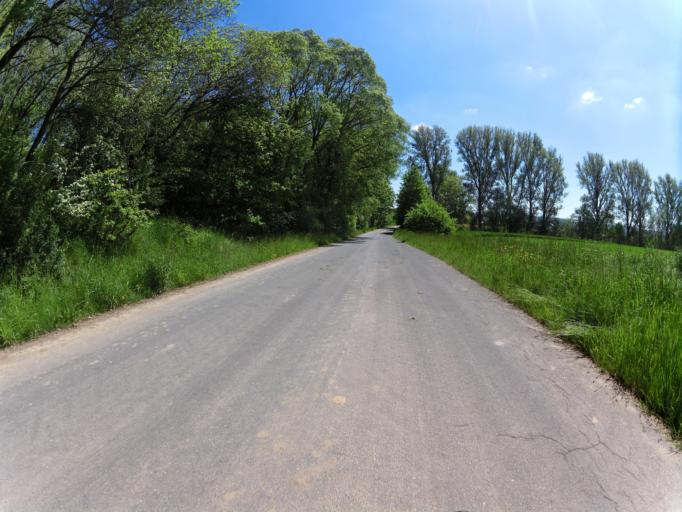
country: DE
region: Thuringia
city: Dankmarshausen
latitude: 50.9547
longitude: 10.0172
